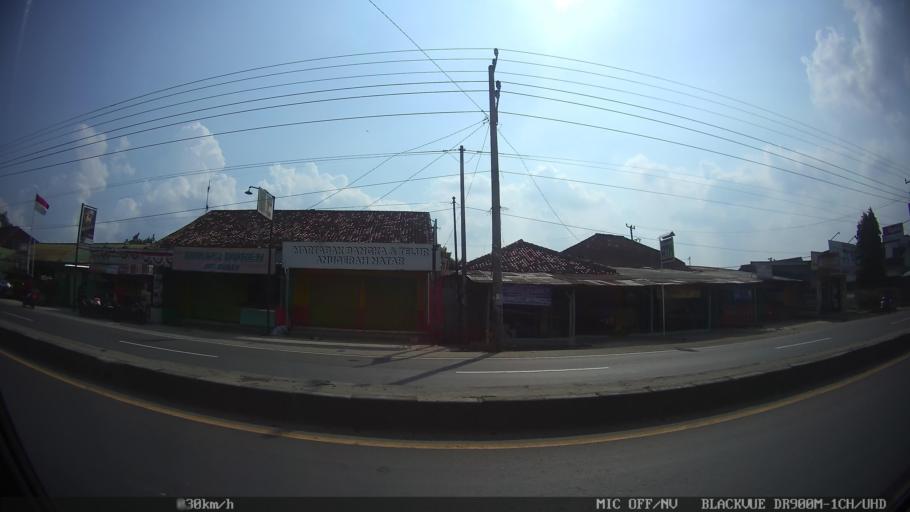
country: ID
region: Lampung
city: Natar
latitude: -5.3154
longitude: 105.1960
